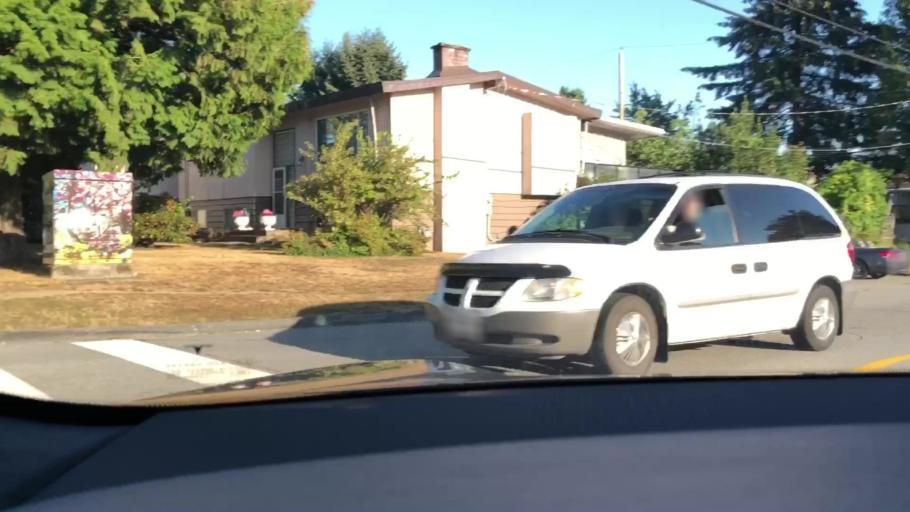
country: CA
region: British Columbia
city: Burnaby
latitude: 49.2752
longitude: -122.9701
